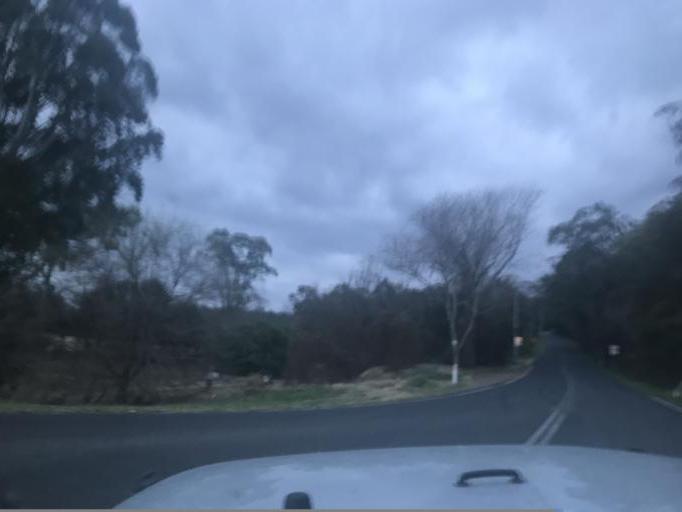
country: AU
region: New South Wales
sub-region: Hawkesbury
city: Pitt Town
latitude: -33.5052
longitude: 150.8747
